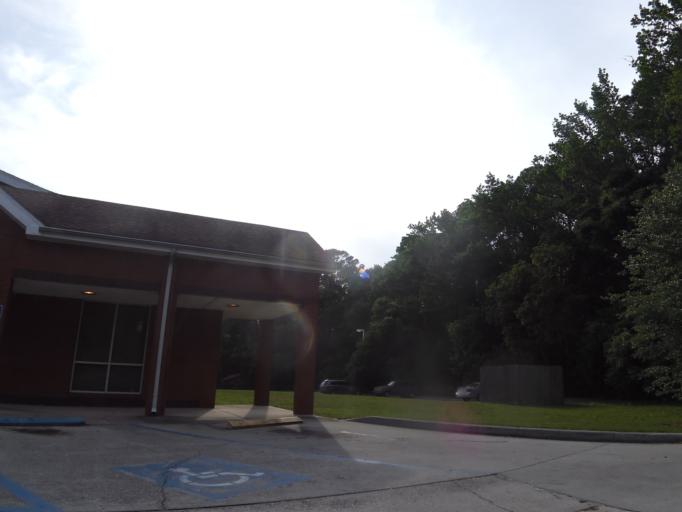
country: US
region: Florida
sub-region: Nassau County
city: Yulee
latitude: 30.6312
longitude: -81.6081
